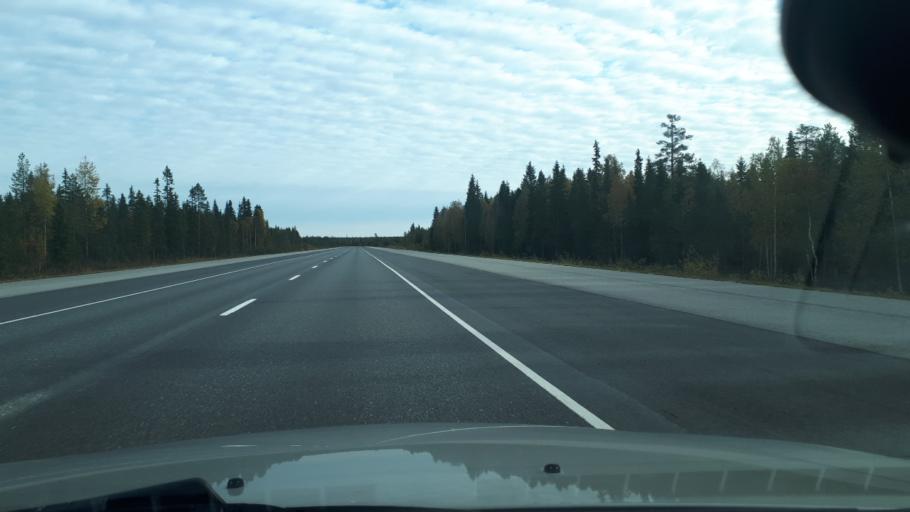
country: FI
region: Northern Ostrobothnia
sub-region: Oulu
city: Yli-Ii
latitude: 65.8969
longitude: 25.7094
